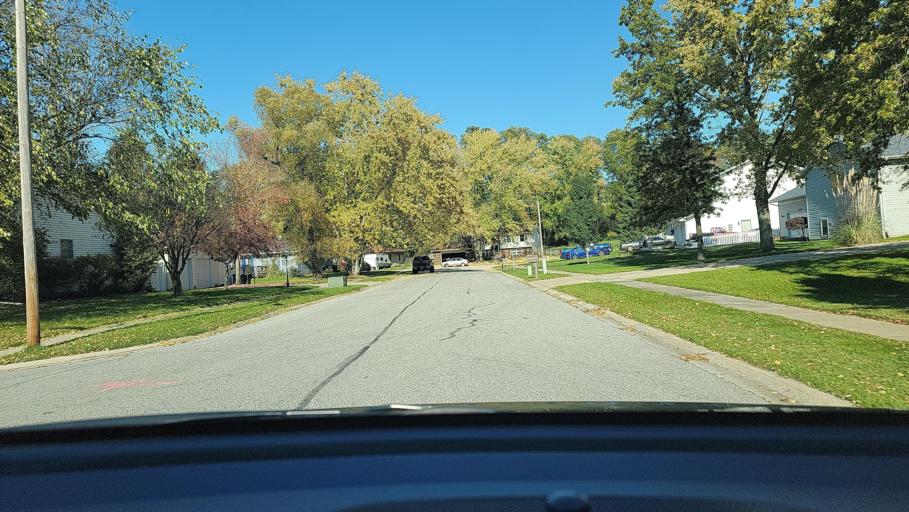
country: US
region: Indiana
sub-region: Porter County
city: Portage
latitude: 41.5807
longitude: -87.1571
